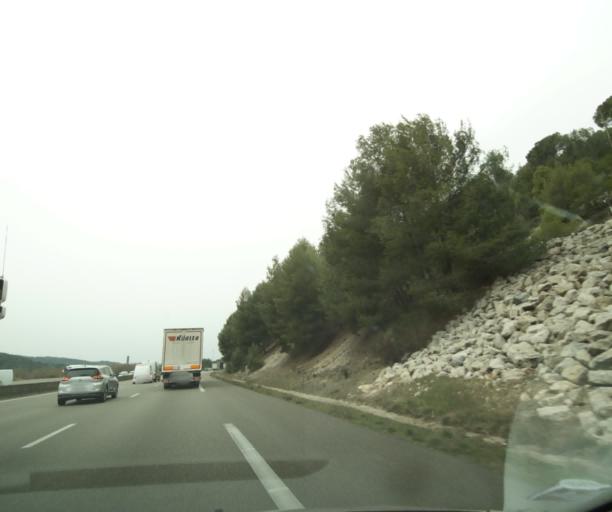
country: FR
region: Provence-Alpes-Cote d'Azur
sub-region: Departement des Bouches-du-Rhone
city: Le Tholonet
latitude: 43.5138
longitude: 5.4878
